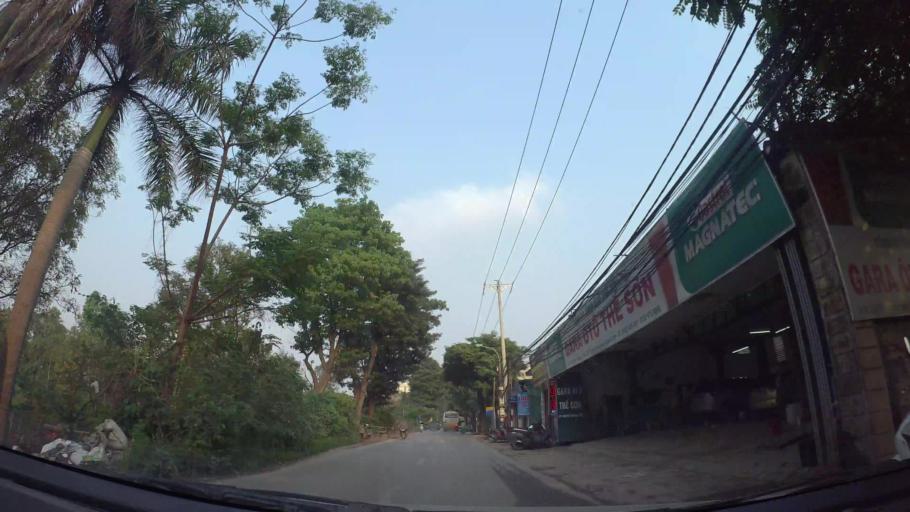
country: VN
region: Ha Noi
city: Tay Ho
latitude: 21.0760
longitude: 105.7942
